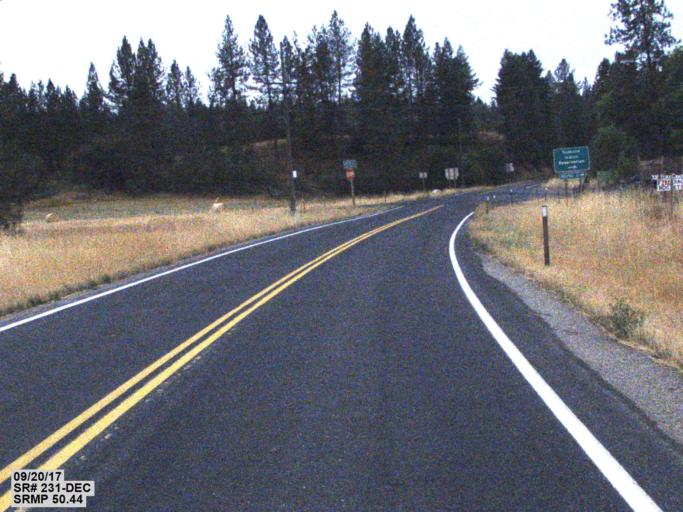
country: US
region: Washington
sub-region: Spokane County
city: Fairchild Air Force Base
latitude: 47.9090
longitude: -117.8056
